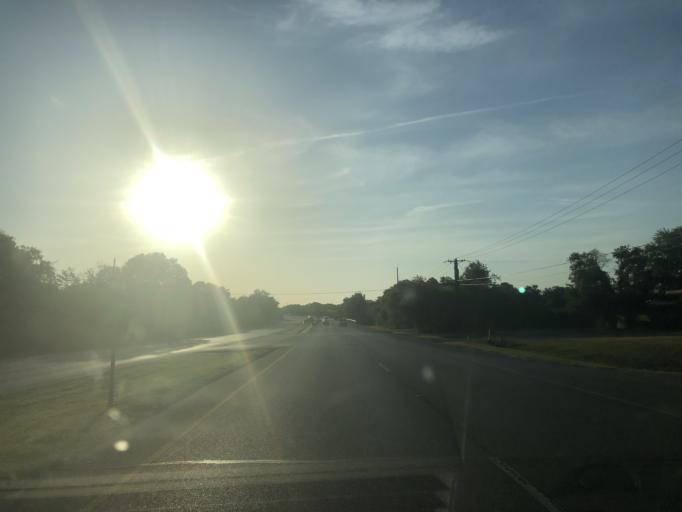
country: US
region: Texas
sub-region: Tarrant County
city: White Settlement
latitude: 32.7205
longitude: -97.5135
